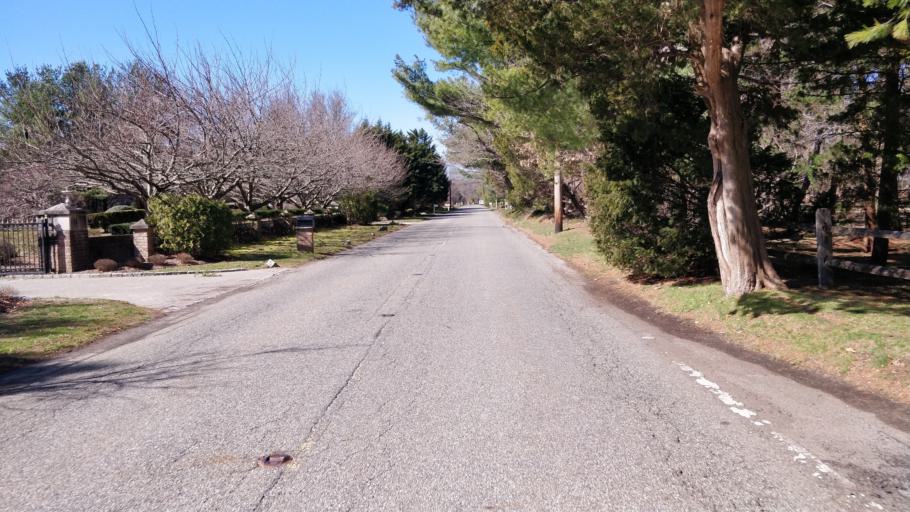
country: US
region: New York
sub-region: Nassau County
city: Woodbury
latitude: 40.8383
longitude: -73.4776
